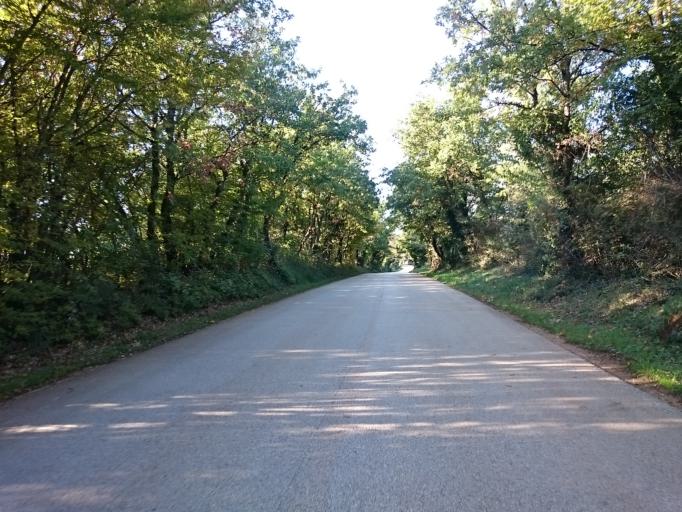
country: HR
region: Istarska
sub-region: Grad Porec
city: Porec
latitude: 45.2784
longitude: 13.6499
